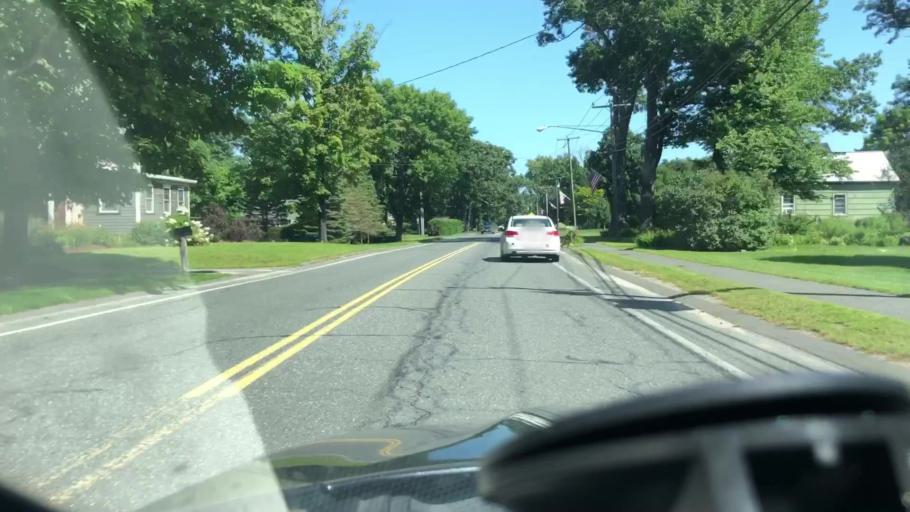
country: US
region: Massachusetts
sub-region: Hampshire County
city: Southampton
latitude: 42.2381
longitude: -72.7255
